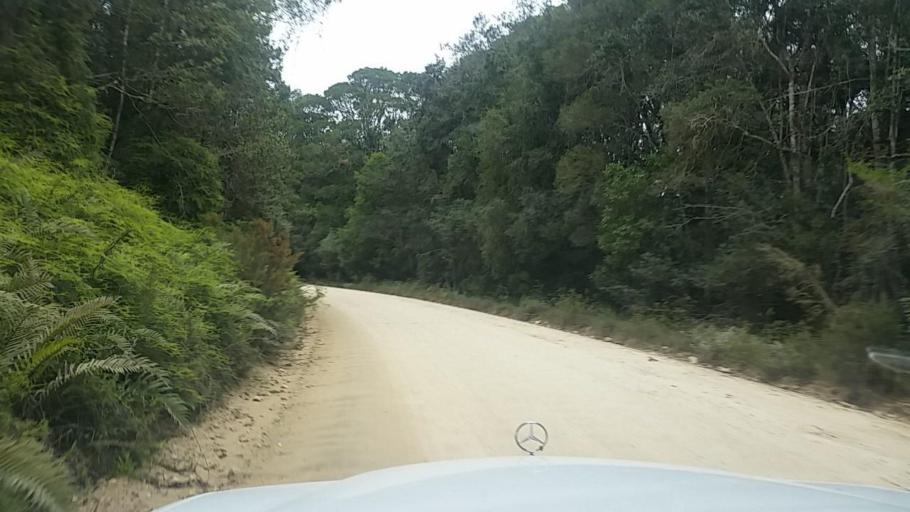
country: ZA
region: Western Cape
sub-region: Eden District Municipality
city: Knysna
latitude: -33.9575
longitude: 23.1553
